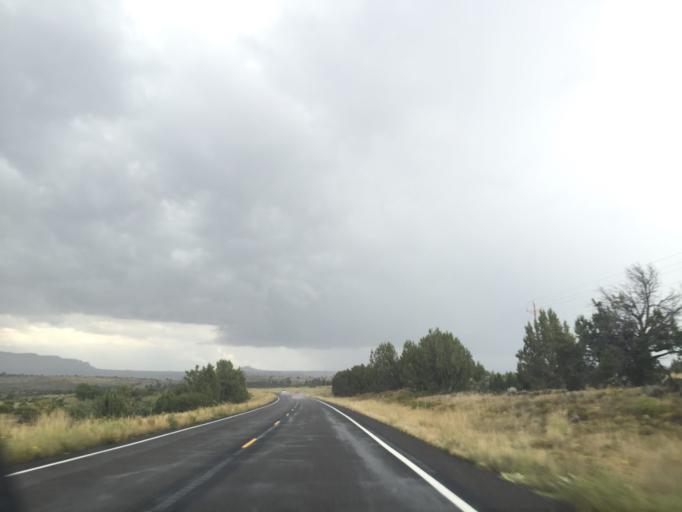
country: US
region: Utah
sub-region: Kane County
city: Kanab
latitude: 37.2409
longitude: -112.7506
